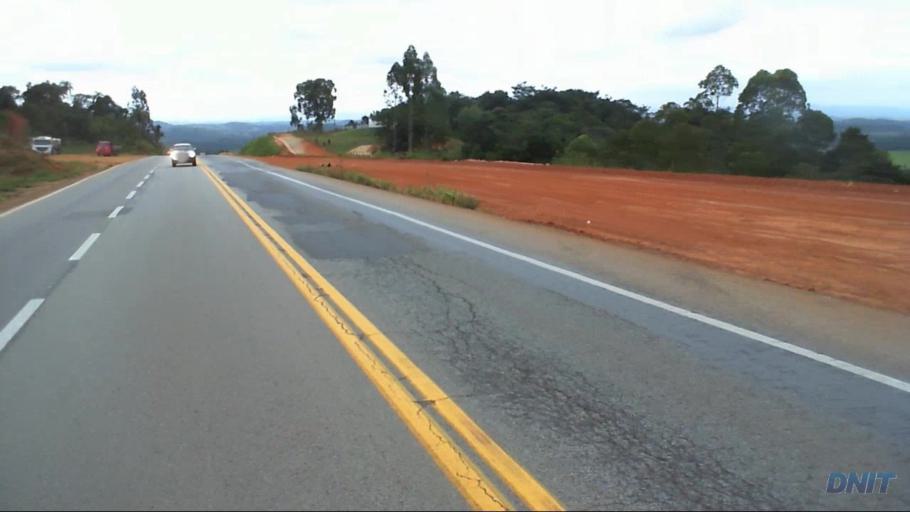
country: BR
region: Minas Gerais
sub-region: Caete
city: Caete
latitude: -19.7501
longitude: -43.5235
